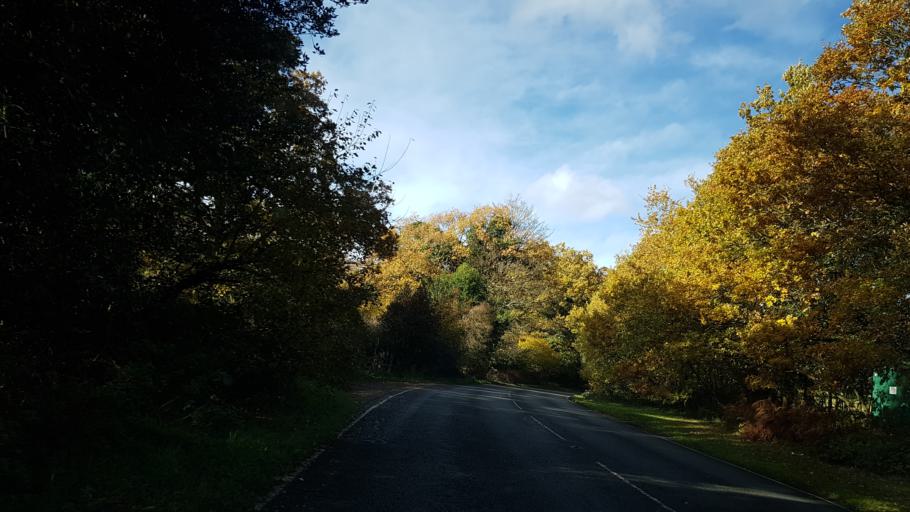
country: GB
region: England
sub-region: Surrey
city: Elstead
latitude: 51.1885
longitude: -0.7164
